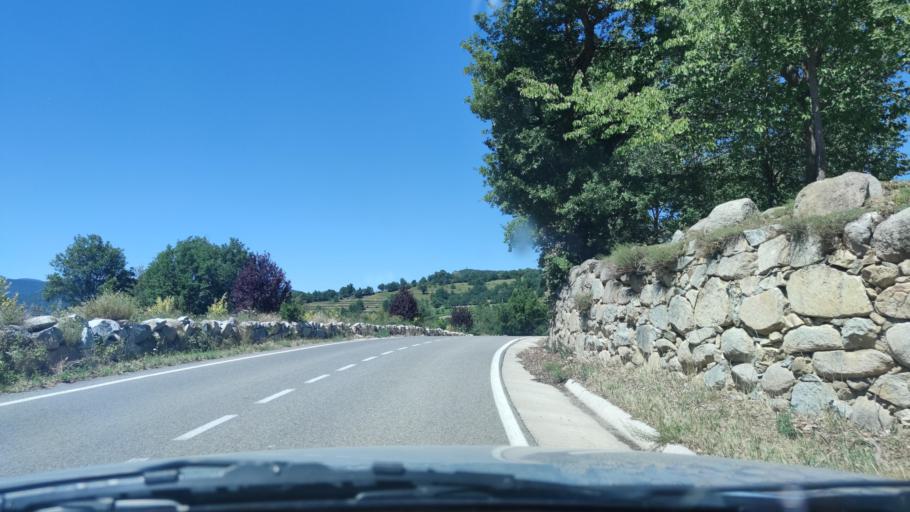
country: ES
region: Catalonia
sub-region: Provincia de Lleida
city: Lles de Cerdanya
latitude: 42.3756
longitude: 1.6845
